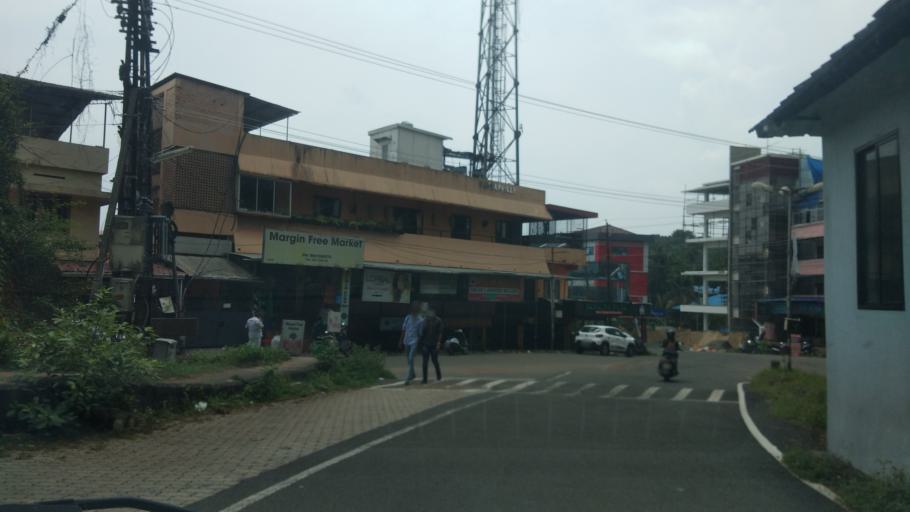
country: IN
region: Kerala
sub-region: Ernakulam
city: Elur
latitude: 10.0451
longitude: 76.3235
